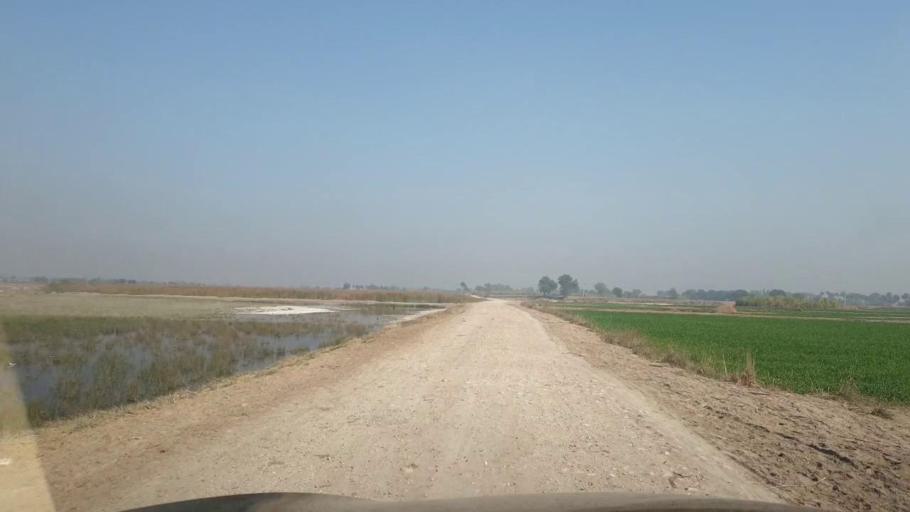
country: PK
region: Sindh
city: Ubauro
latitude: 28.1288
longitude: 69.7510
